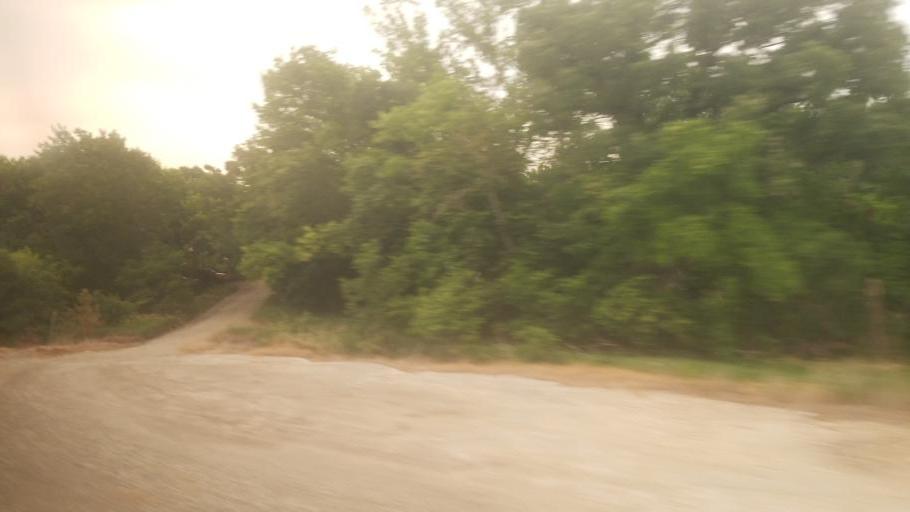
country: US
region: Kansas
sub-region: Chase County
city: Cottonwood Falls
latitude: 38.3997
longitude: -96.5753
